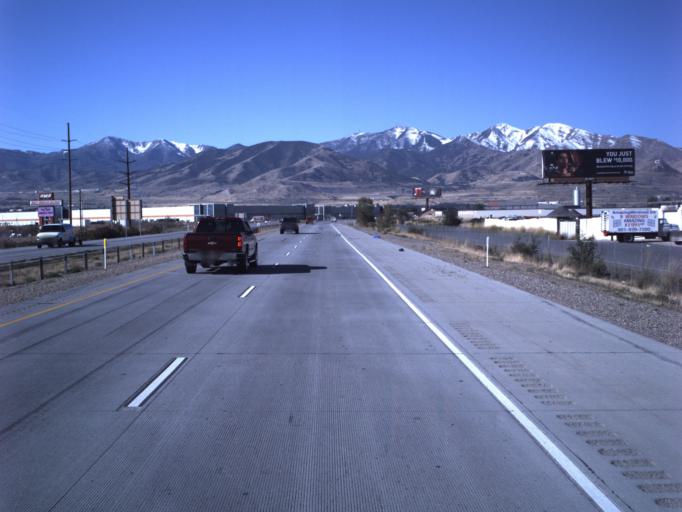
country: US
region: Utah
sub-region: Salt Lake County
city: Magna
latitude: 40.7218
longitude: -112.0478
